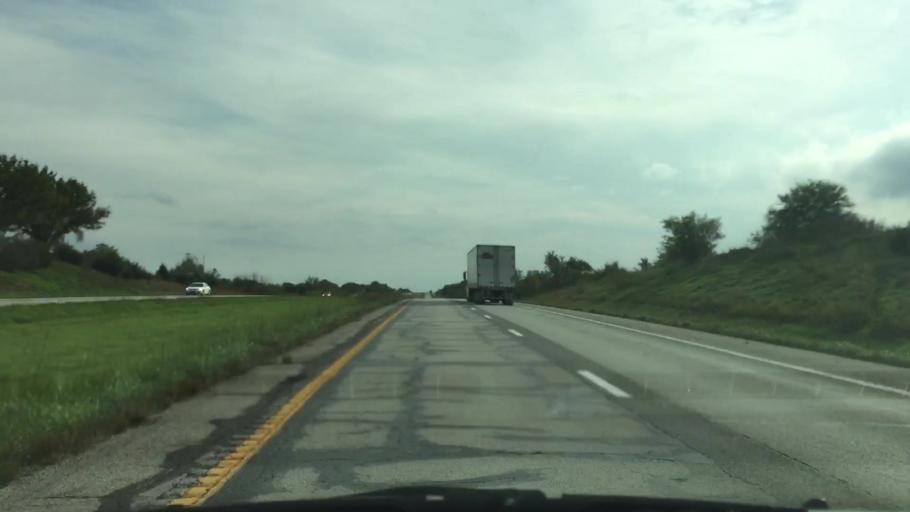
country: US
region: Missouri
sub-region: Harrison County
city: Bethany
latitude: 40.4424
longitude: -93.9840
